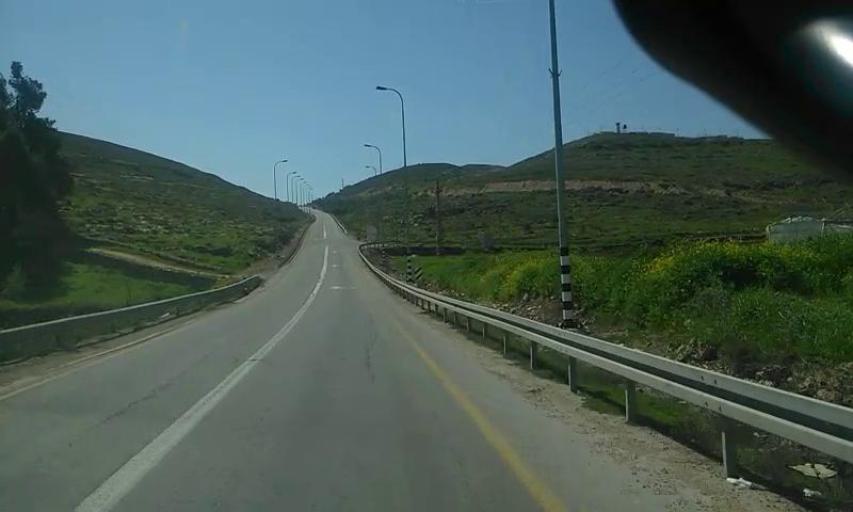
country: PS
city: Khursa
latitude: 31.4808
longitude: 35.0473
